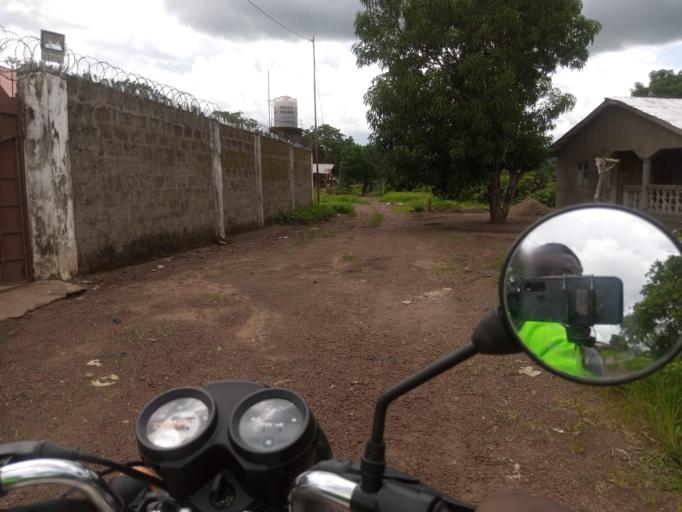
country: SL
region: Northern Province
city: Port Loko
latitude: 8.7768
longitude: -12.7739
